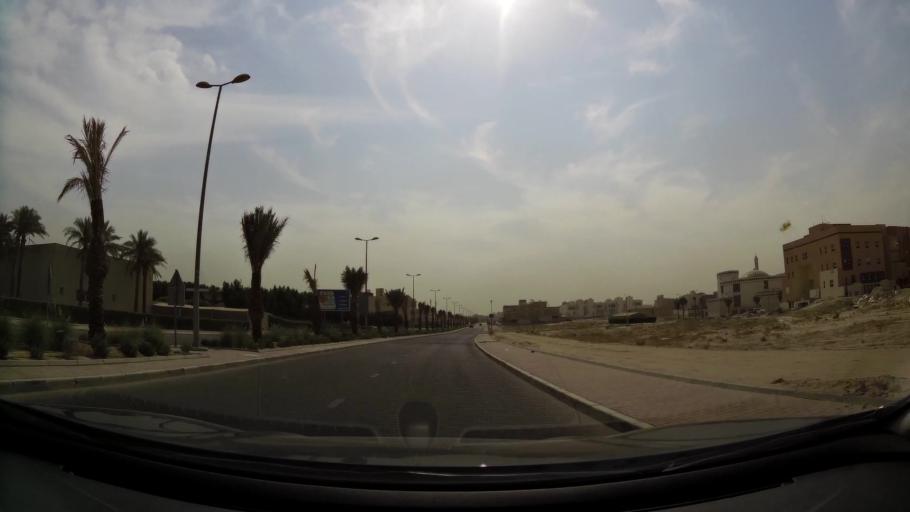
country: KW
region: Al Farwaniyah
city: Janub as Surrah
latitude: 29.2969
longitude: 47.9970
